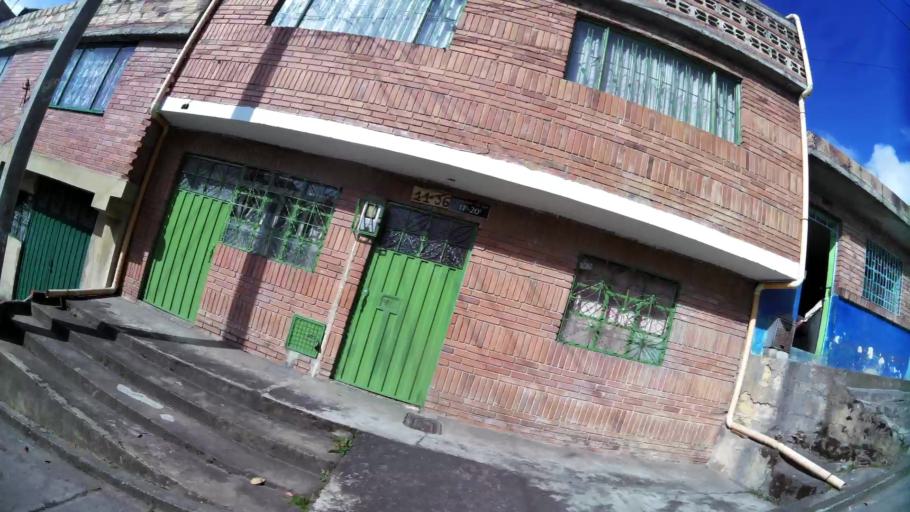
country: CO
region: Bogota D.C.
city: Bogota
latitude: 4.5388
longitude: -74.0893
